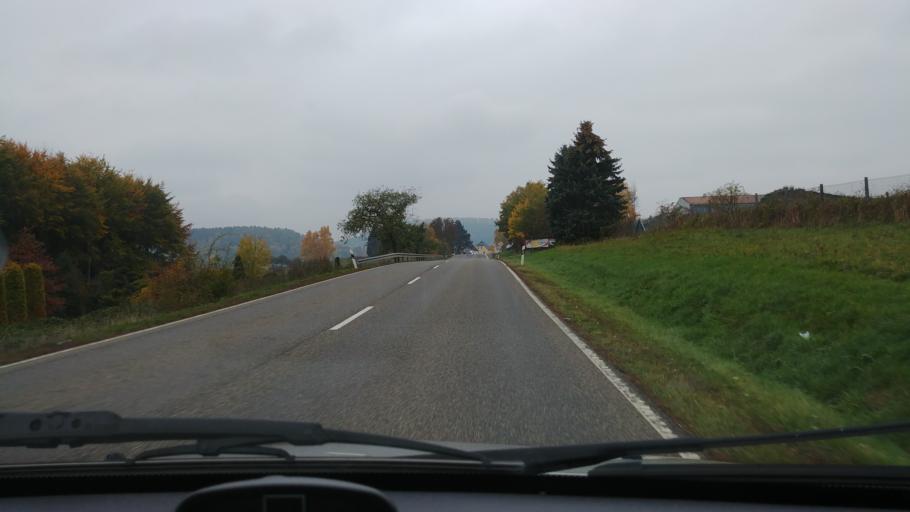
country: DE
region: Rheinland-Pfalz
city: Irmtraut
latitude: 50.5315
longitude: 8.0496
